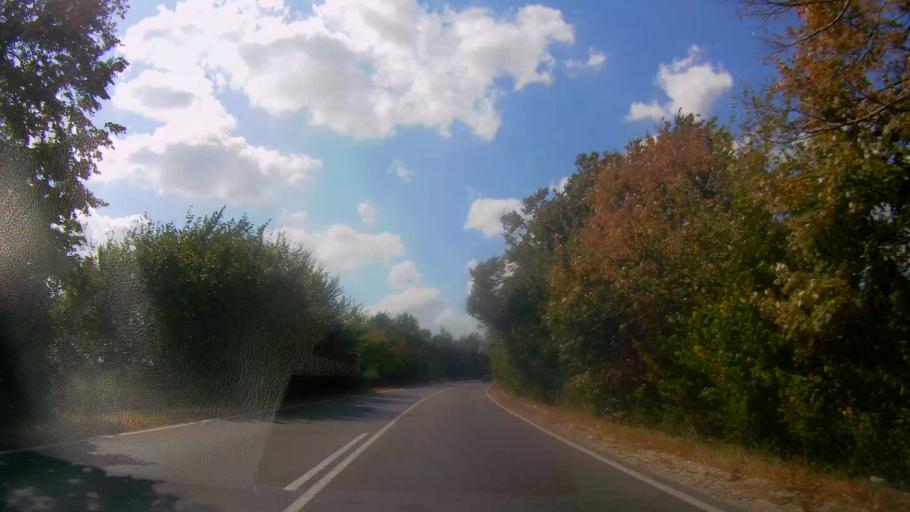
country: BG
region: Ruse
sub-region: Obshtina Ivanovo
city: Ivanovo
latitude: 43.7121
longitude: 25.9196
